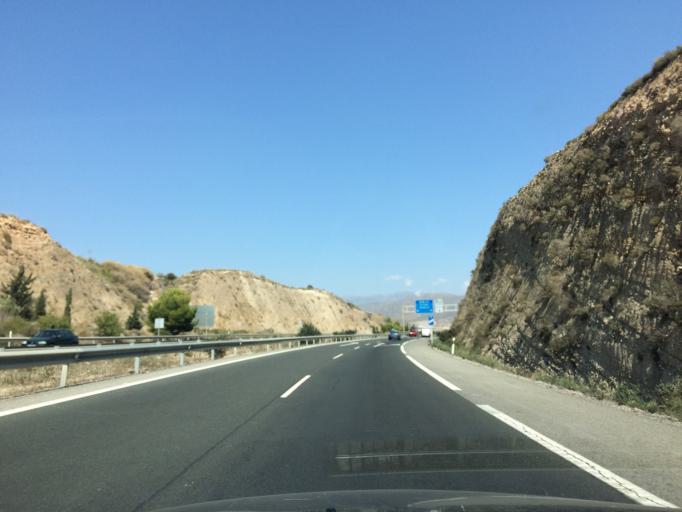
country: ES
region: Andalusia
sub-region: Provincia de Almeria
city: Adra
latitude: 36.7638
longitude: -2.9907
